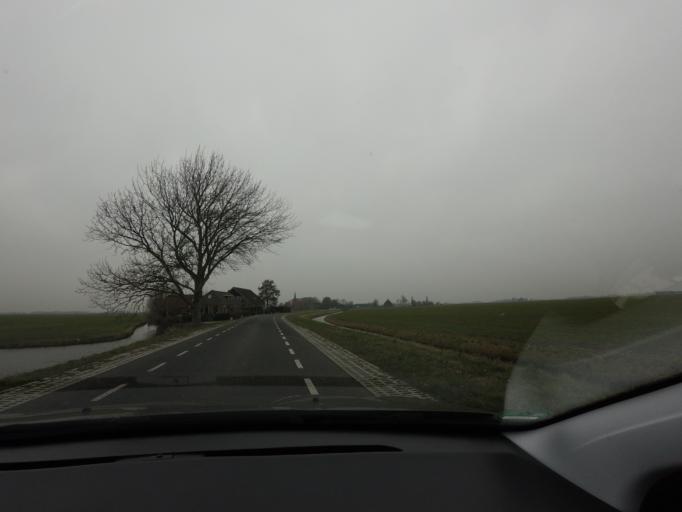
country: NL
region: Friesland
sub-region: Sudwest Fryslan
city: Bolsward
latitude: 53.1060
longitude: 5.5426
